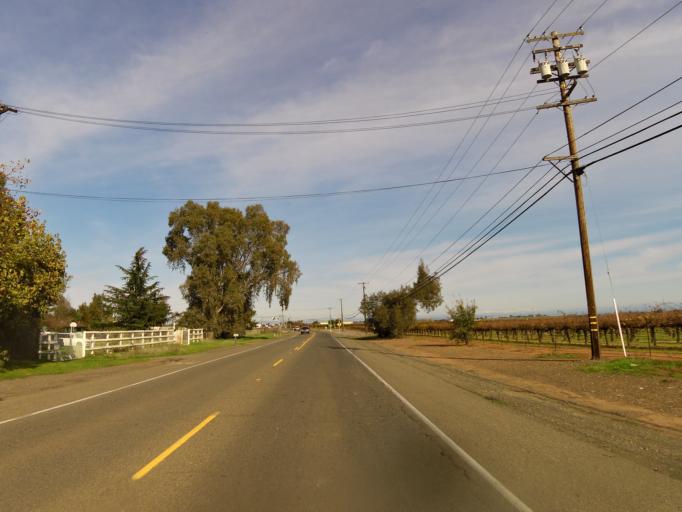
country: US
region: California
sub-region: Sacramento County
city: Wilton
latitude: 38.4500
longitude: -121.2794
